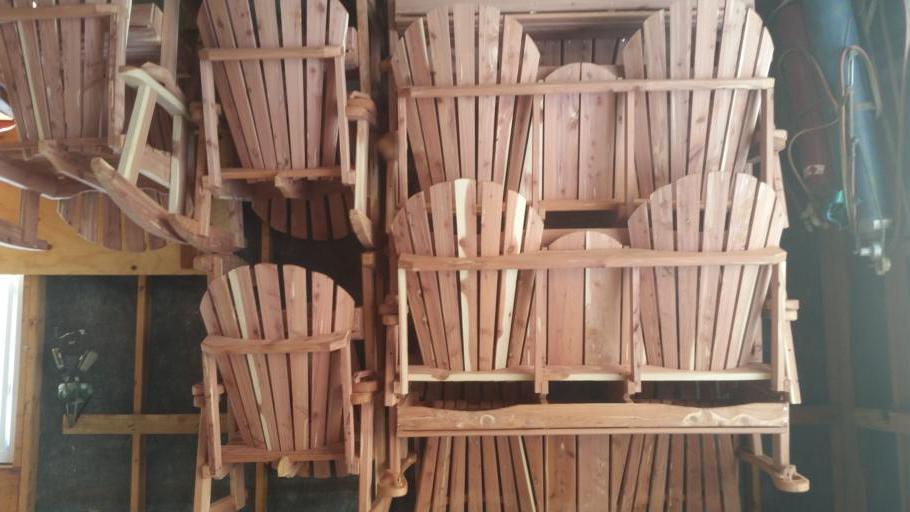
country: US
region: Ohio
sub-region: Gallia County
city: Gallipolis
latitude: 38.8813
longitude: -82.3302
